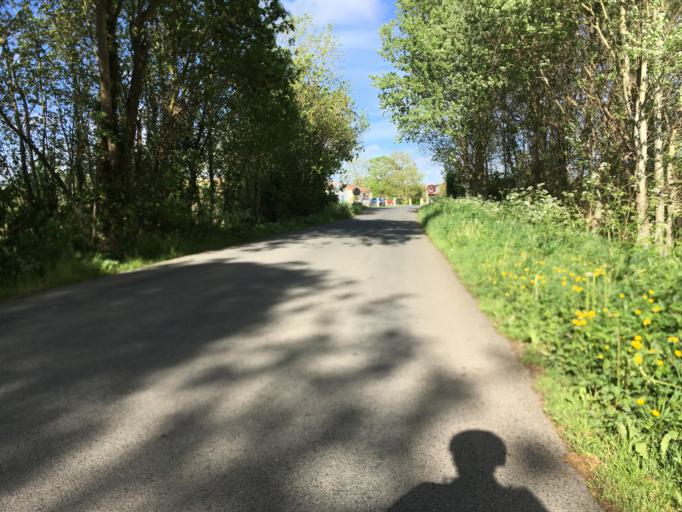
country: FR
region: Poitou-Charentes
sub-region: Departement de la Charente-Maritime
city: Verines
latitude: 46.1789
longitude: -0.9206
